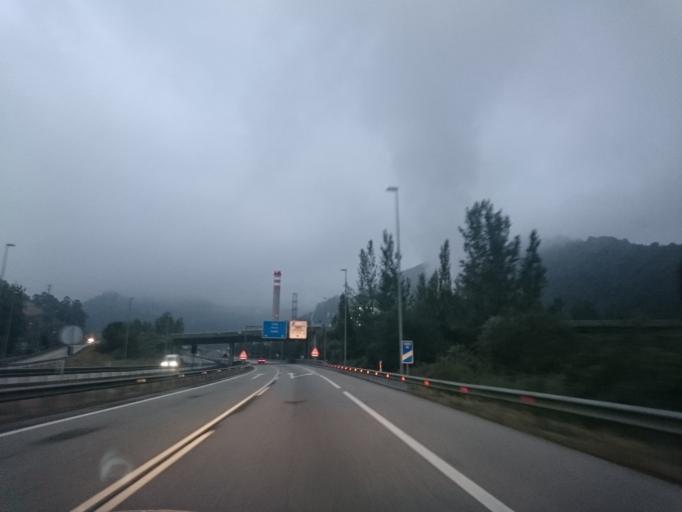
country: ES
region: Asturias
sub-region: Province of Asturias
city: Mieres
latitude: 43.2775
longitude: -5.8097
